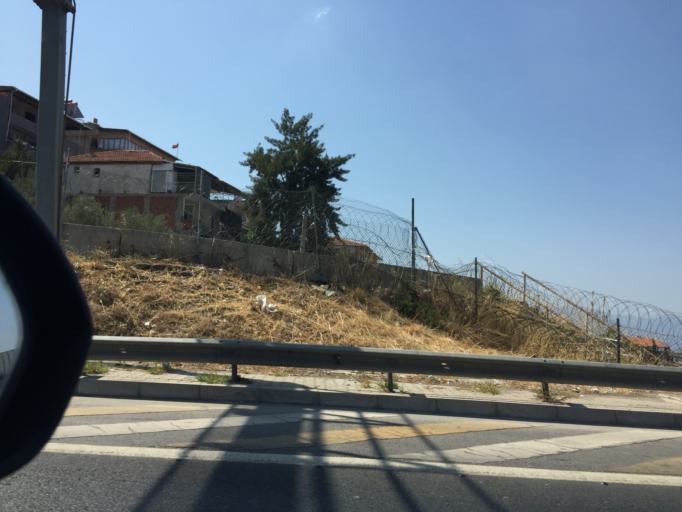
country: TR
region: Izmir
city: Karsiyaka
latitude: 38.4851
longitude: 27.1387
